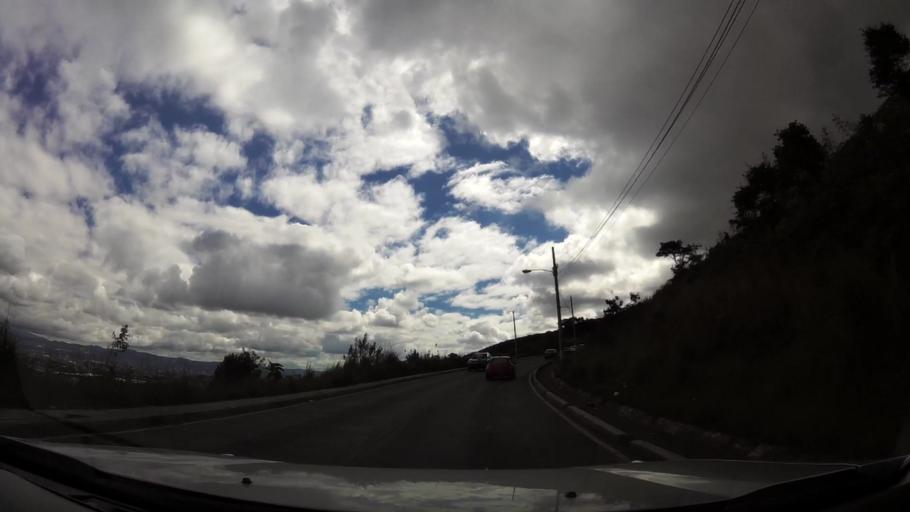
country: GT
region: Guatemala
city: Guatemala City
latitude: 14.6643
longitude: -90.5513
